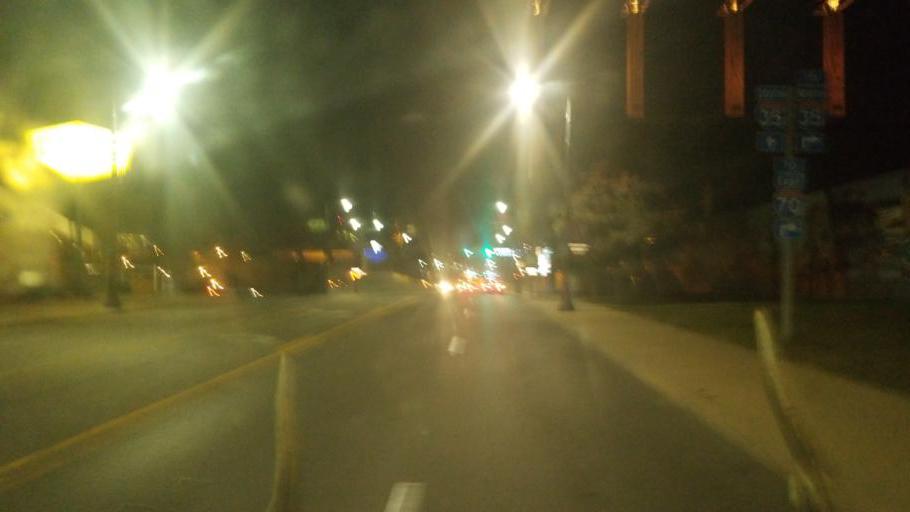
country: US
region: Missouri
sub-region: Jackson County
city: Kansas City
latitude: 39.0950
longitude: -94.5886
